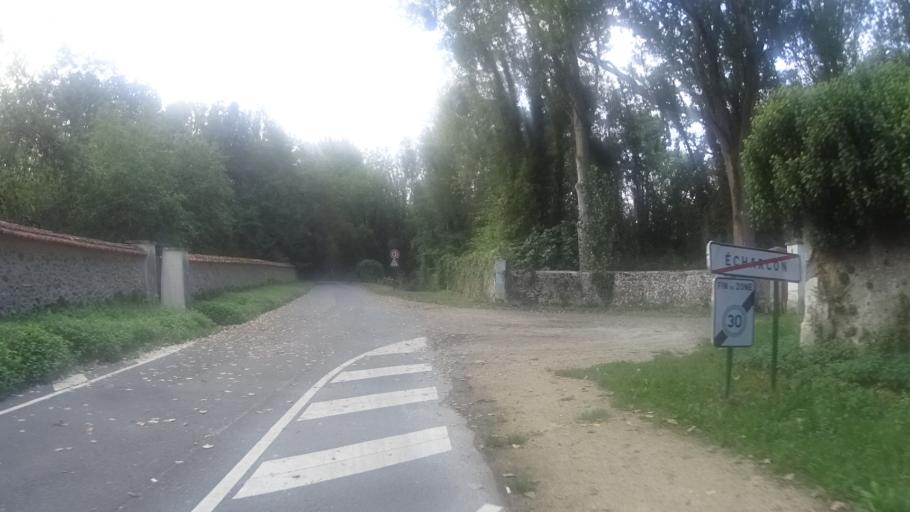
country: FR
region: Ile-de-France
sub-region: Departement de l'Essonne
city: Mennecy
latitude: 48.5675
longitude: 2.4153
